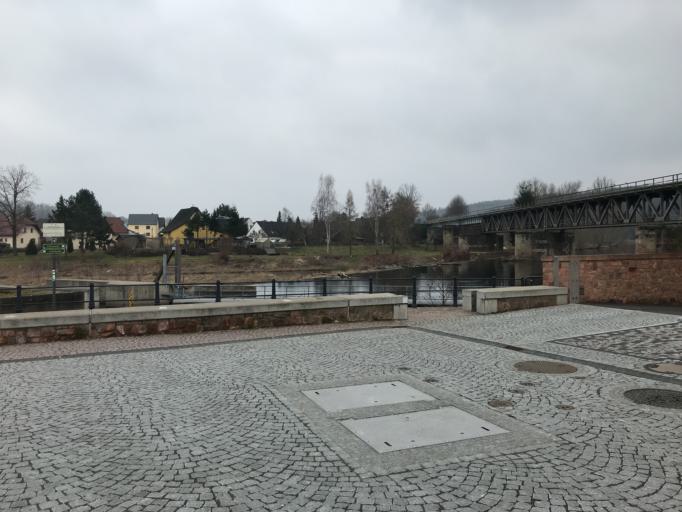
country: DE
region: Saxony
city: Rochlitz
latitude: 51.0454
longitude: 12.7942
